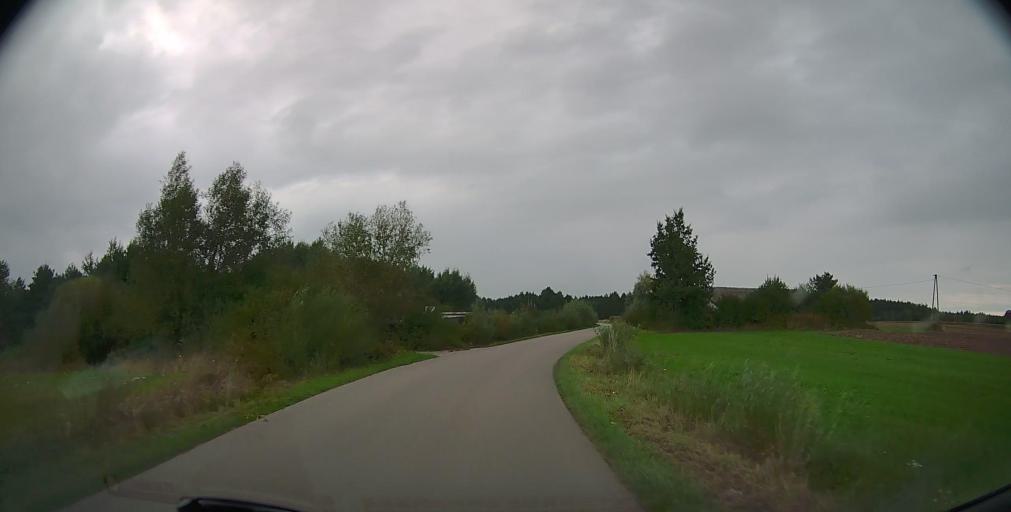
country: PL
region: Masovian Voivodeship
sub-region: Powiat radomski
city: Jedlinsk
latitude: 51.4565
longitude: 21.1034
